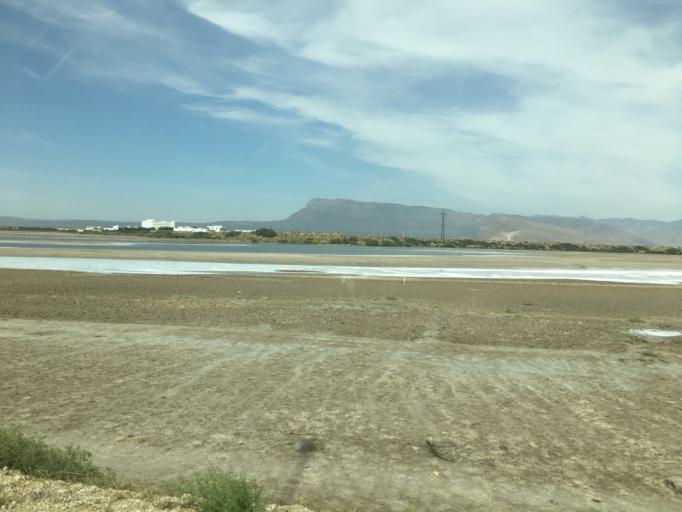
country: TM
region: Balkan
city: Balkanabat
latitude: 39.6191
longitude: 54.1632
